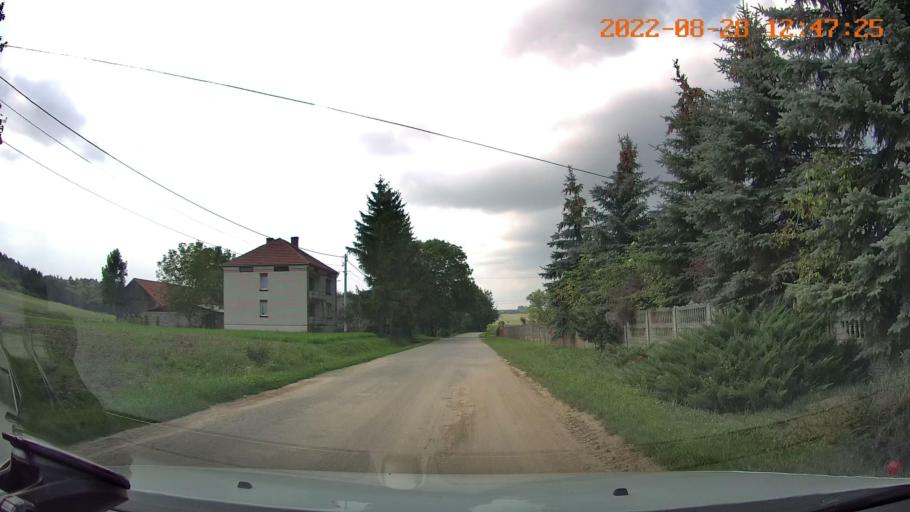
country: PL
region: Swietokrzyskie
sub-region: Powiat pinczowski
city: Dzialoszyce
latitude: 50.3580
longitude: 20.3092
